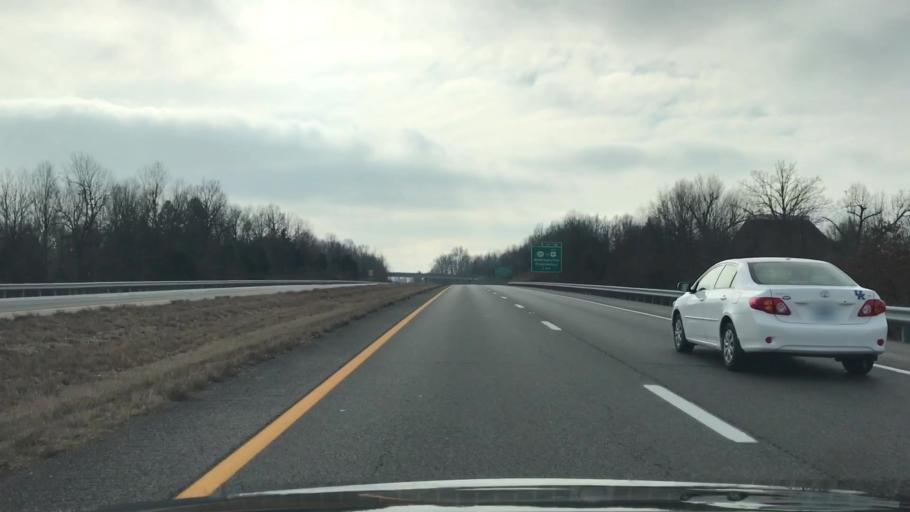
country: US
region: Kentucky
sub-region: Hopkins County
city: Madisonville
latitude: 37.3698
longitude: -87.4888
